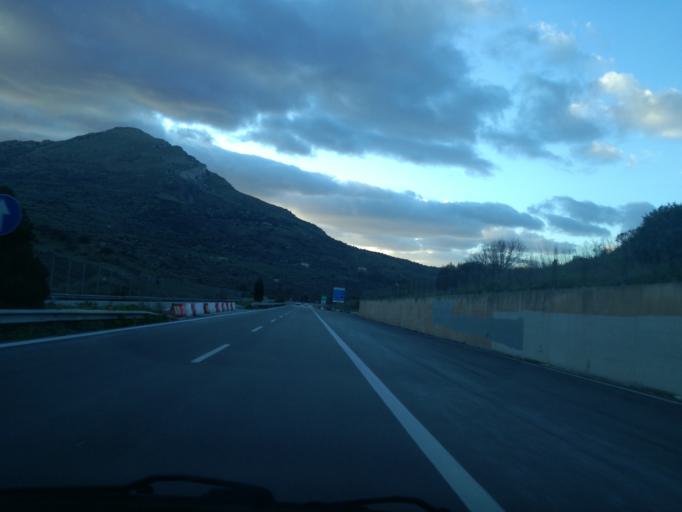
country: IT
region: Sicily
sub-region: Palermo
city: Scillato
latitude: 37.8360
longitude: 13.9347
